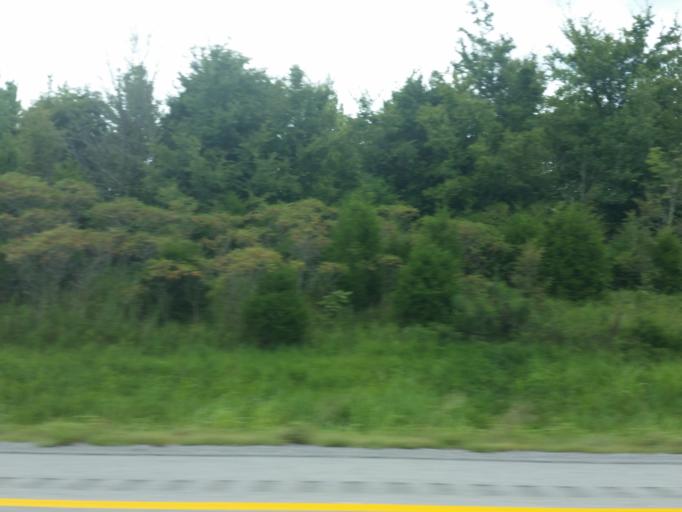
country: US
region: Kentucky
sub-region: Caldwell County
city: Princeton
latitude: 36.9987
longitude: -87.9590
